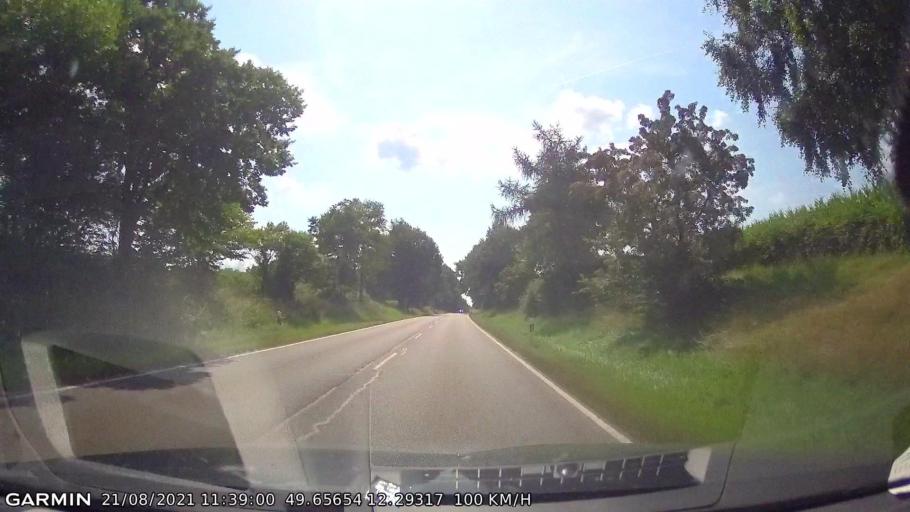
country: DE
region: Bavaria
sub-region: Upper Palatinate
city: Waldthurn
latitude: 49.6565
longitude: 12.2932
